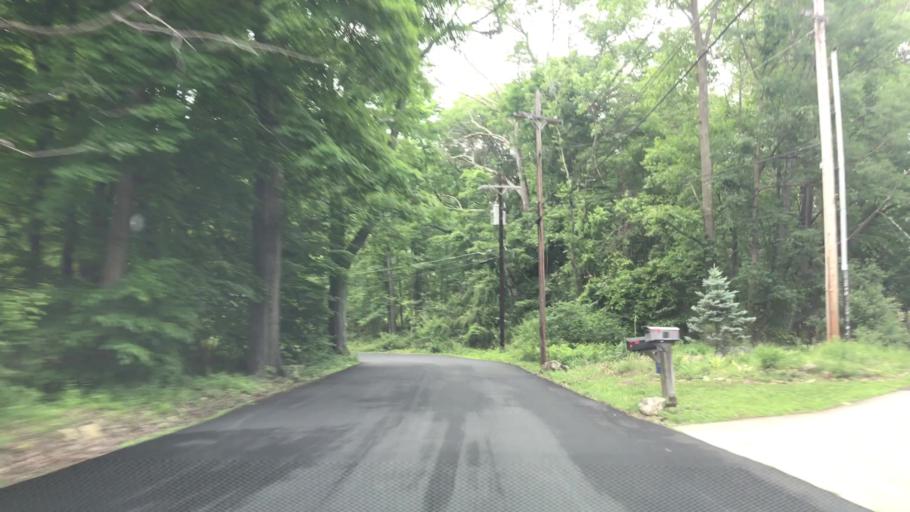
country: US
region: New Jersey
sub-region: Hunterdon County
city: Lebanon
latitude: 40.6603
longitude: -74.8330
